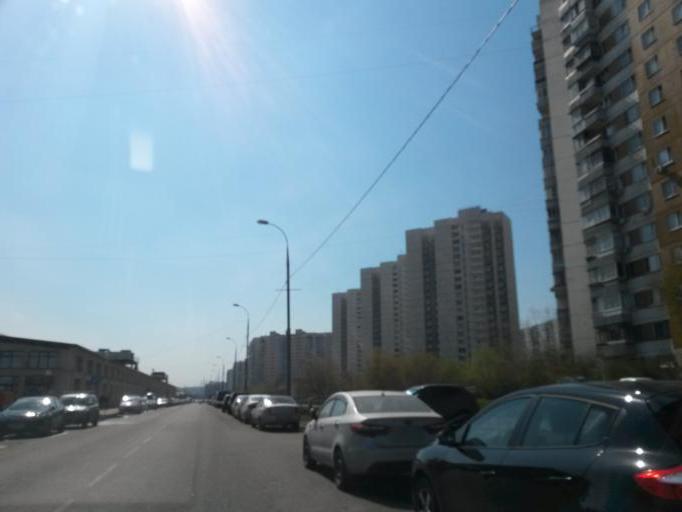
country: RU
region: Moscow
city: Mar'ino
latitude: 55.6537
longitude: 37.7411
